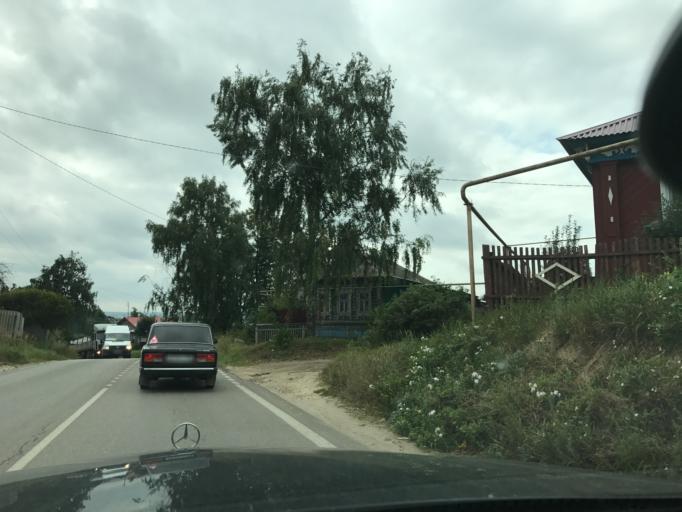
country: RU
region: Nizjnij Novgorod
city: Pavlovo
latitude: 55.9949
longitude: 43.0423
